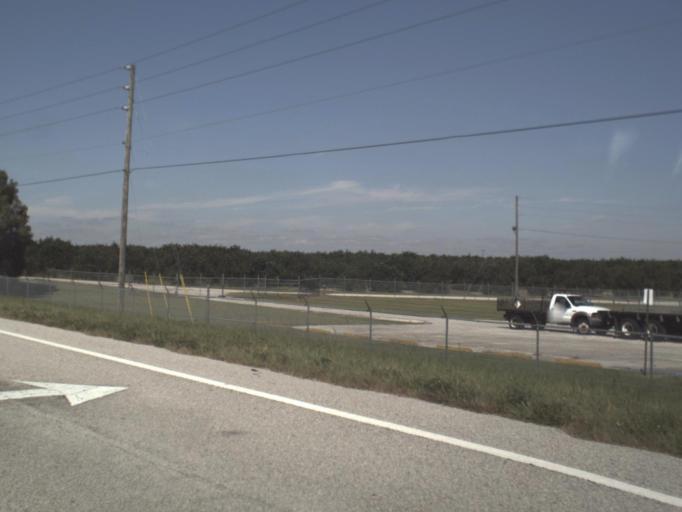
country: US
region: Florida
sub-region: Highlands County
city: Lake Placid
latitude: 27.3539
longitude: -81.3885
